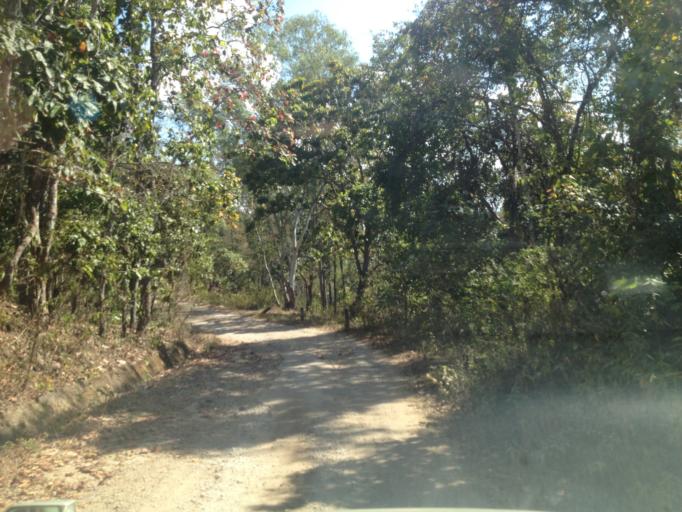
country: TH
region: Mae Hong Son
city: Ban Huai I Huak
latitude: 18.1074
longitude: 98.1818
